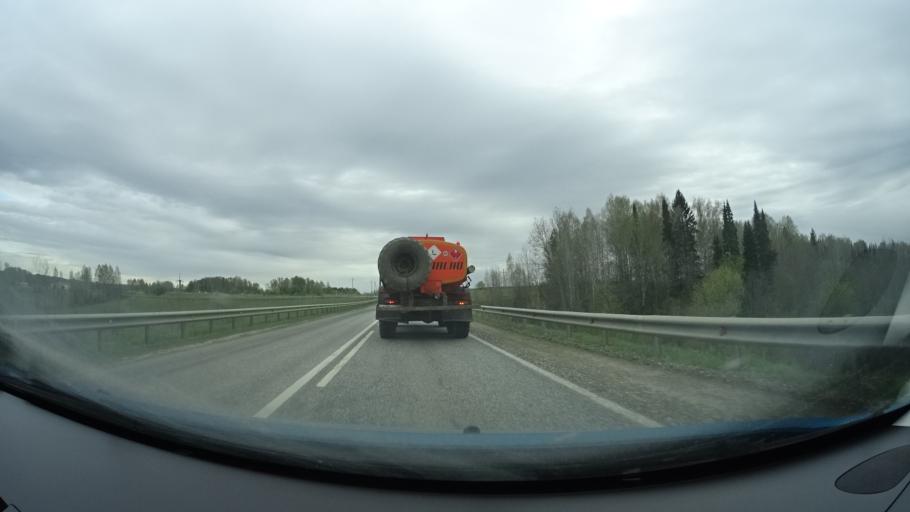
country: RU
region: Perm
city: Osa
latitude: 57.1610
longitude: 55.5305
